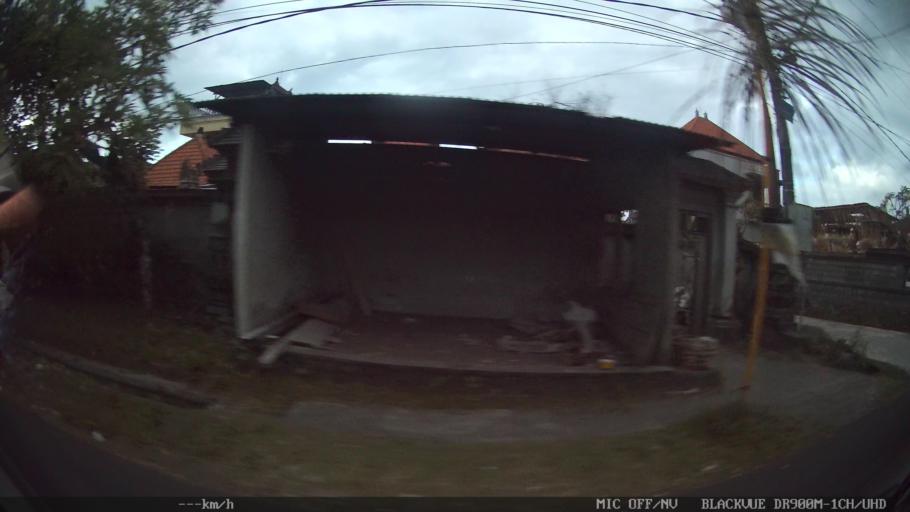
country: ID
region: Bali
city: Banjar Pasekan
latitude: -8.6292
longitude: 115.2857
